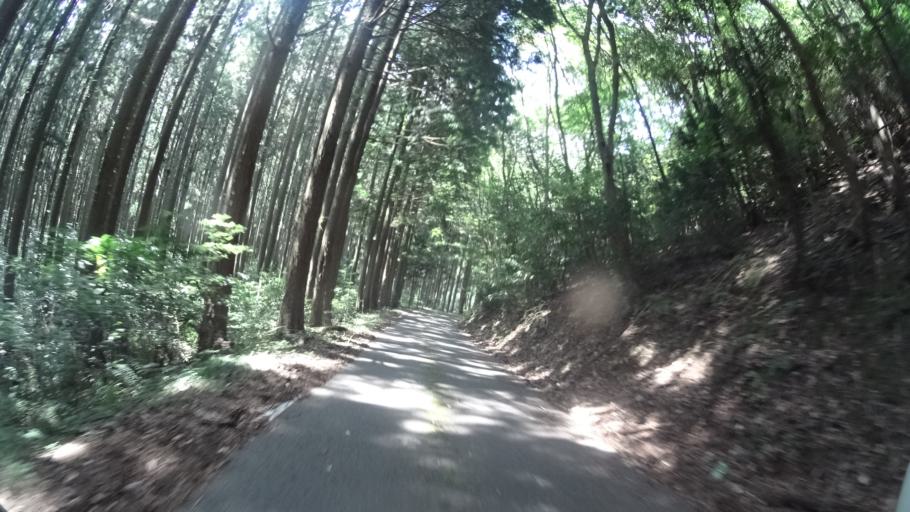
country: JP
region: Yamaguchi
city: Hagi
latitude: 34.4953
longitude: 131.5603
